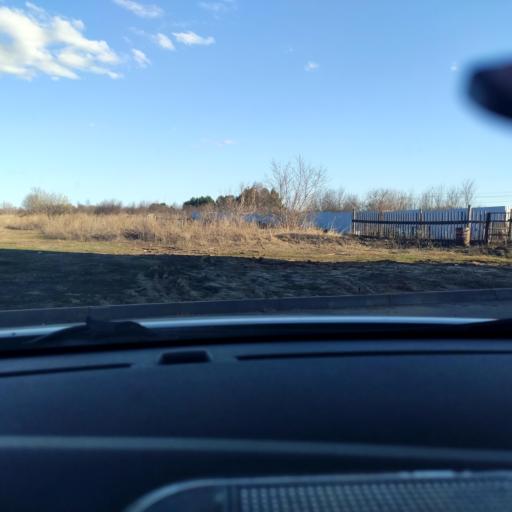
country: RU
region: Tatarstan
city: Vysokaya Gora
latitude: 55.8850
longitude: 49.2697
